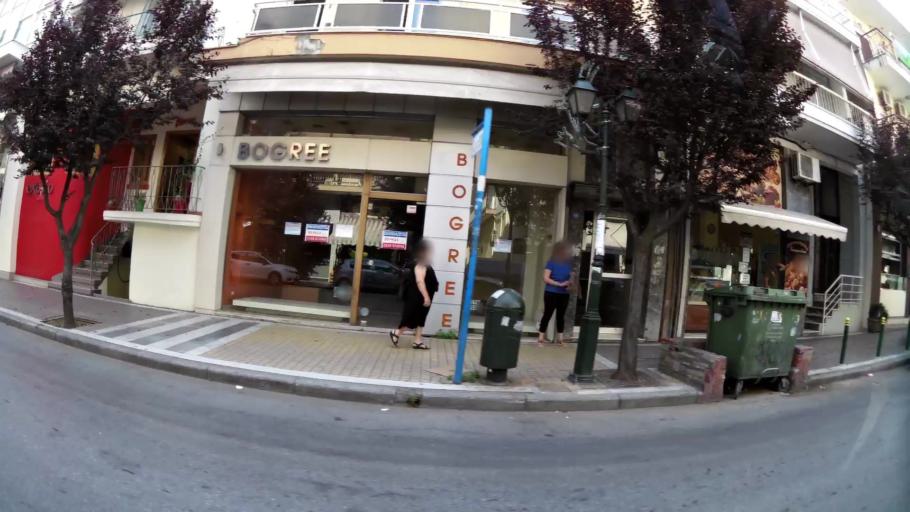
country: GR
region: Central Macedonia
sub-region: Nomos Thessalonikis
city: Sykies
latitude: 40.6540
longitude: 22.9392
